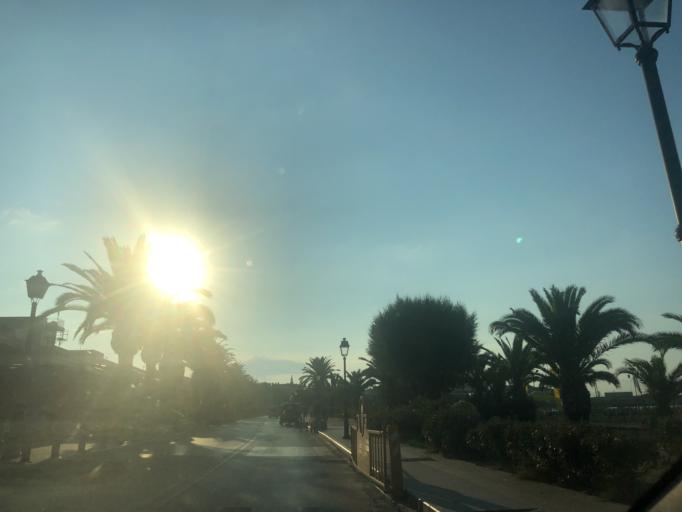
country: GR
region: Crete
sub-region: Nomos Rethymnis
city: Rethymno
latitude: 35.3671
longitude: 24.4799
